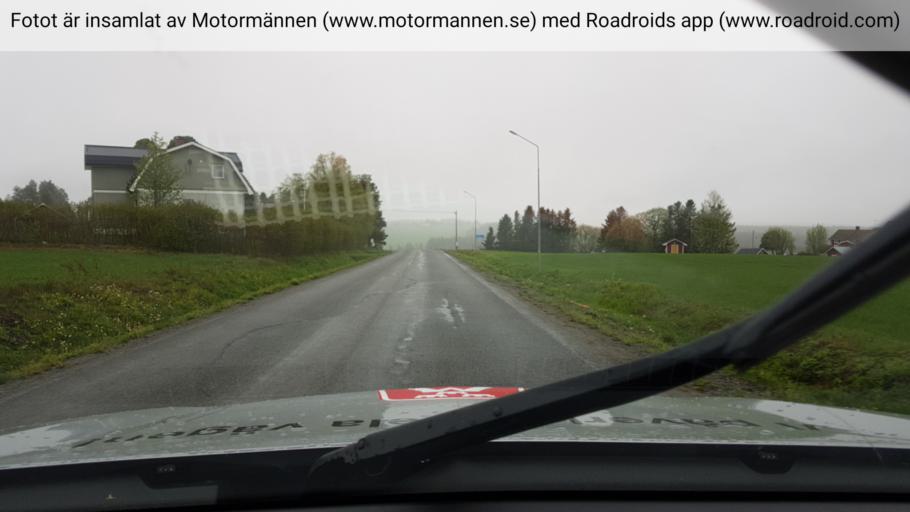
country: SE
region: Jaemtland
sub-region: Bergs Kommun
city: Hoverberg
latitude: 62.9914
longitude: 14.3257
